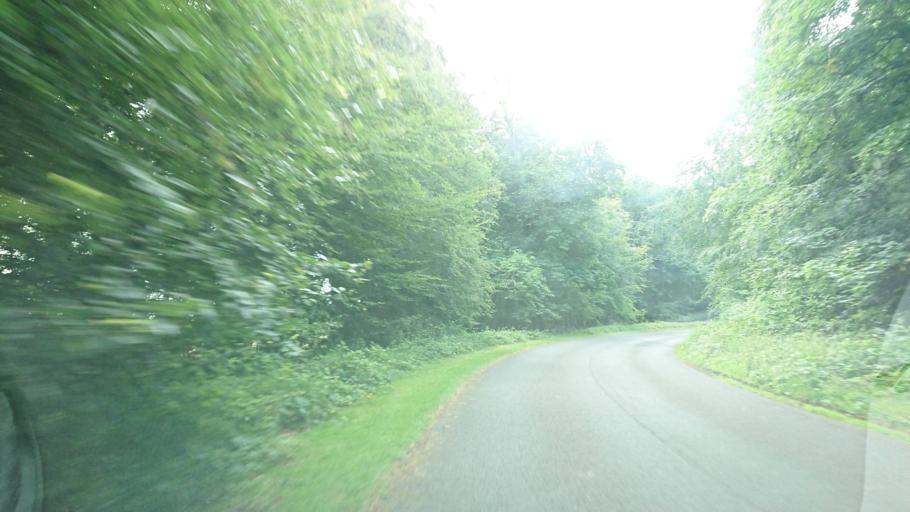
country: IE
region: Connaught
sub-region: Roscommon
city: Boyle
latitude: 53.9767
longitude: -8.2418
